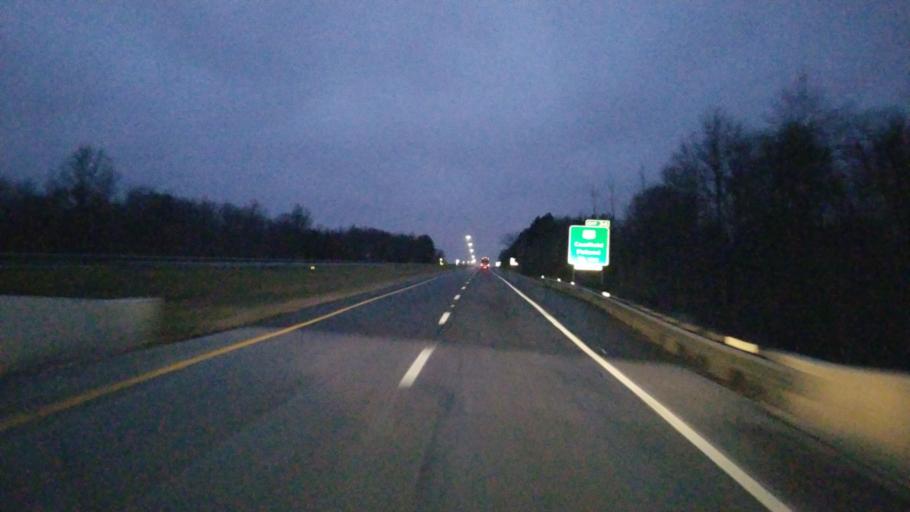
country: US
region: Ohio
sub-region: Mahoning County
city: Canfield
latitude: 41.0130
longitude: -80.7392
